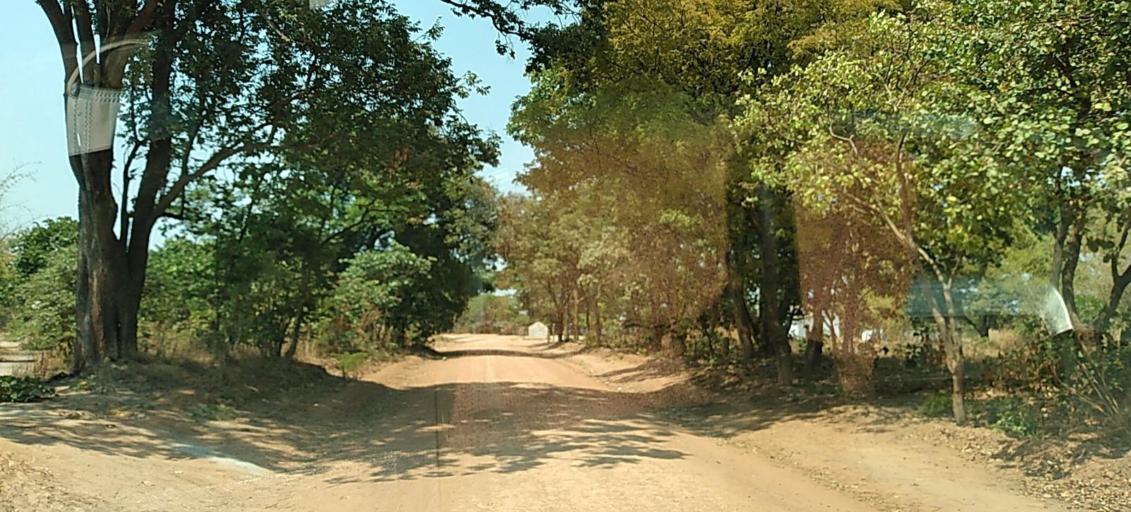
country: ZM
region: Copperbelt
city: Chambishi
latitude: -12.6024
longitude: 27.9640
